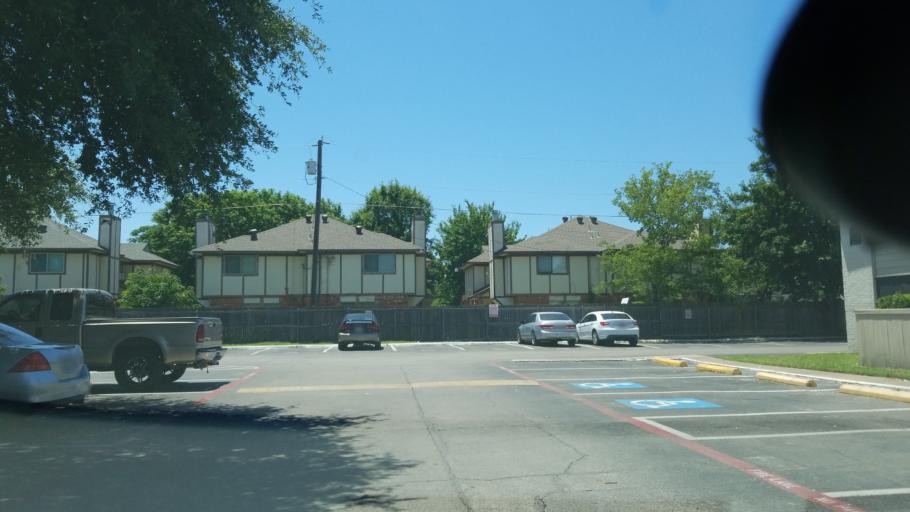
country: US
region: Texas
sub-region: Dallas County
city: Irving
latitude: 32.8267
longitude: -96.9365
